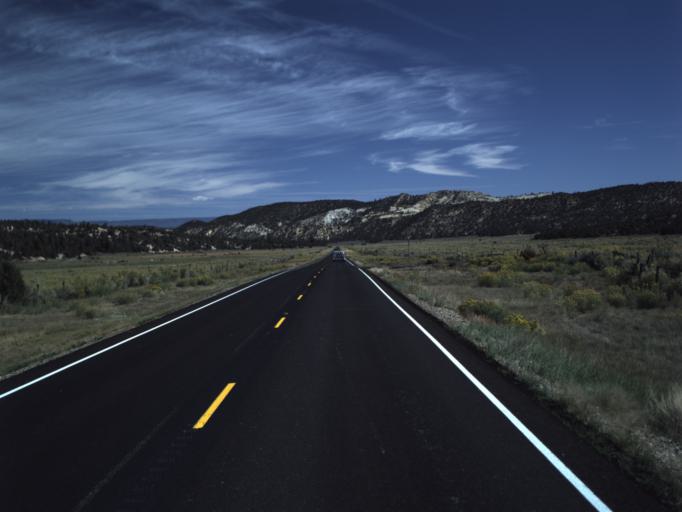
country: US
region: Utah
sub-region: Garfield County
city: Panguitch
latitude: 37.6821
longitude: -111.8143
